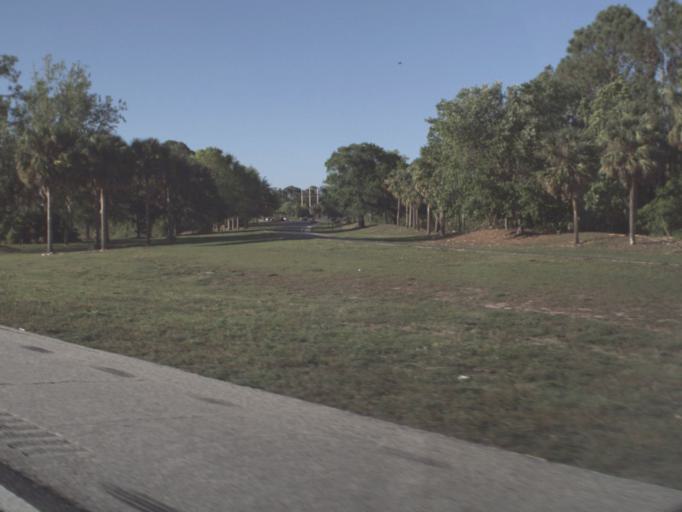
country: US
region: Florida
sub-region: Flagler County
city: Palm Coast
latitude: 29.5497
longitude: -81.2158
